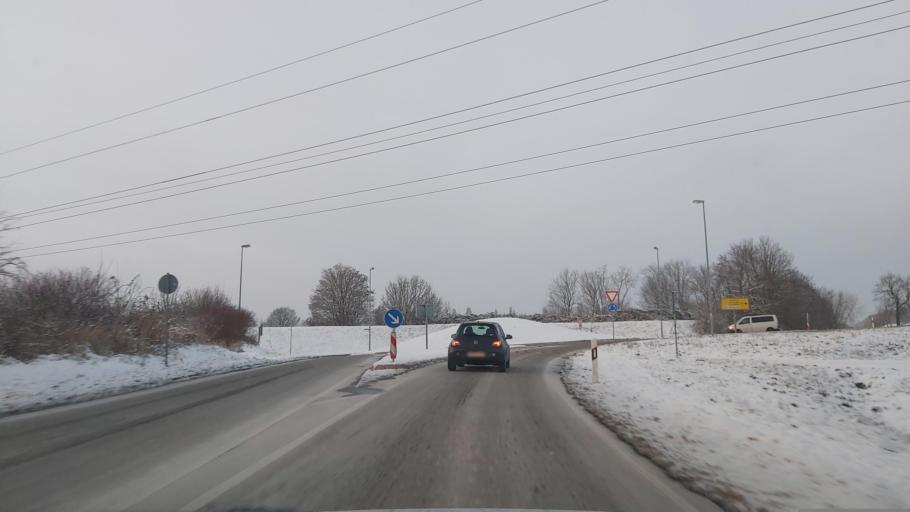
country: DE
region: Baden-Wuerttemberg
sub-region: Tuebingen Region
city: Metzingen
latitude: 48.5505
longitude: 9.2899
